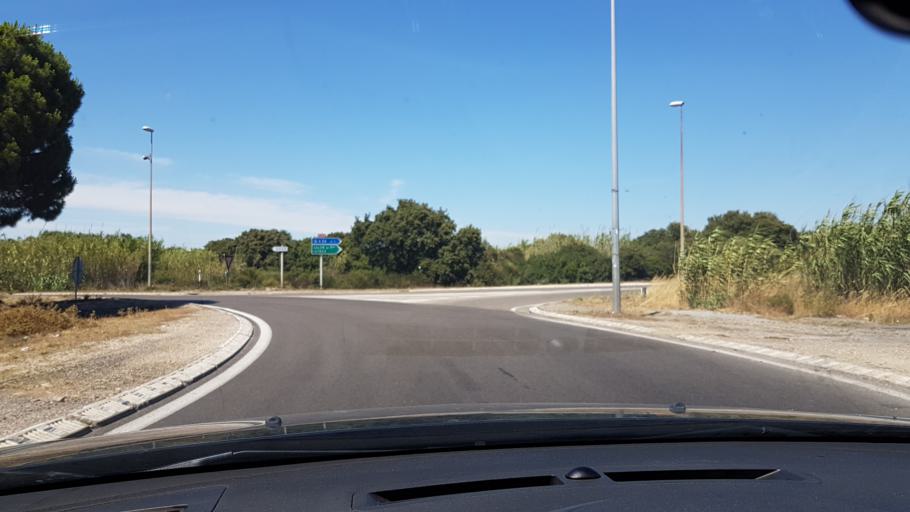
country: FR
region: Provence-Alpes-Cote d'Azur
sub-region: Departement des Bouches-du-Rhone
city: Fos-sur-Mer
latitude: 43.4614
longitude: 4.9199
